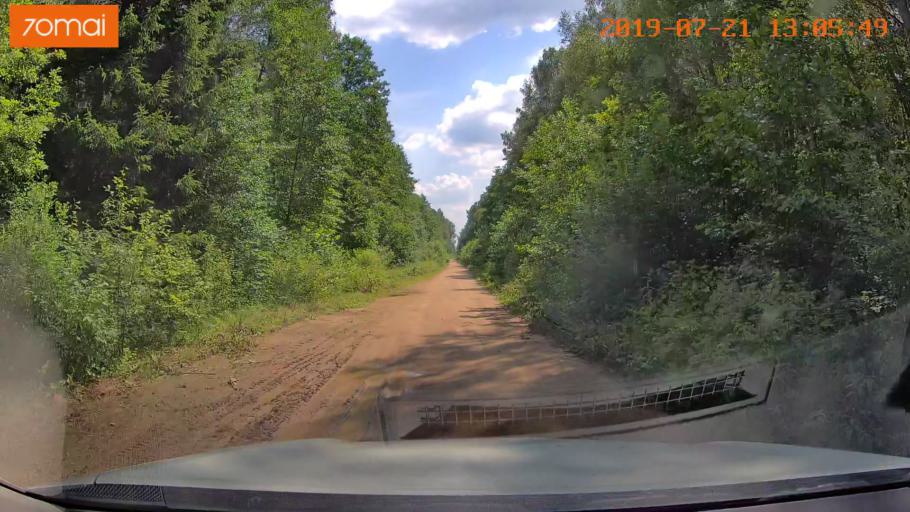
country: BY
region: Grodnenskaya
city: Lyubcha
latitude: 53.8308
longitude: 26.0389
